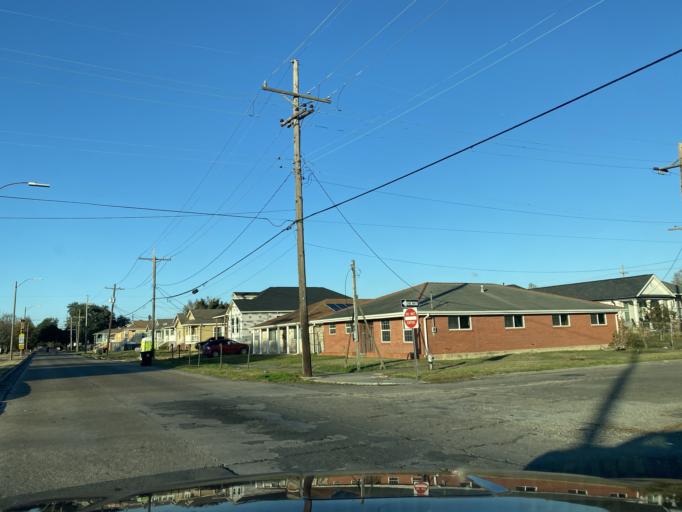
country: US
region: Louisiana
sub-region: Orleans Parish
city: New Orleans
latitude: 30.0173
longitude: -90.0514
